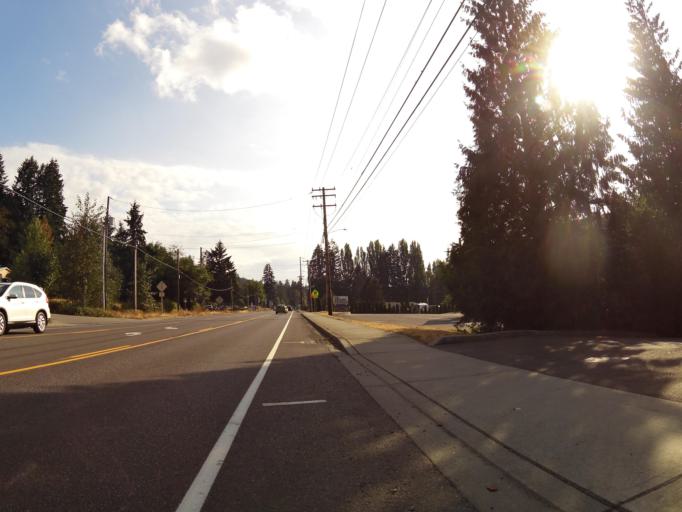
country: US
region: Washington
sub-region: Mason County
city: Belfair
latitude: 47.4415
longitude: -122.8336
